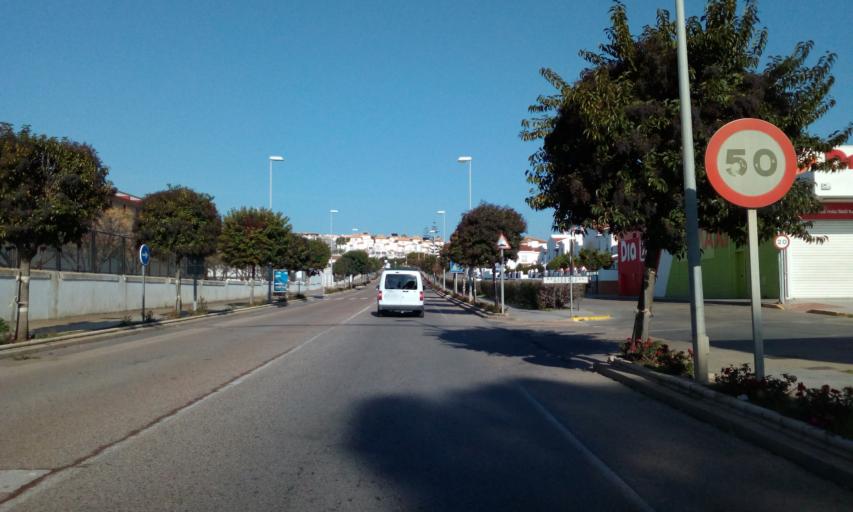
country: ES
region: Andalusia
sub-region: Provincia de Huelva
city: Ayamonte
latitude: 37.2166
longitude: -7.3942
